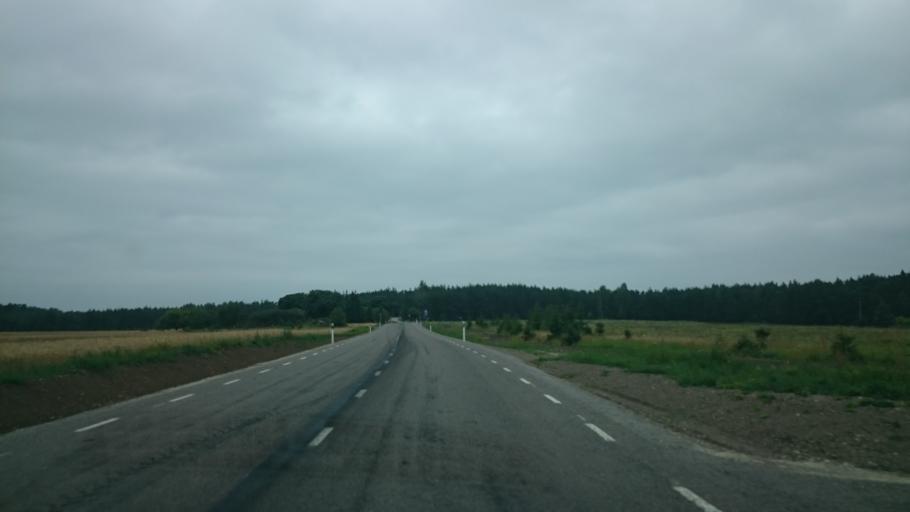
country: EE
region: Saare
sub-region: Orissaare vald
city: Orissaare
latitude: 58.5856
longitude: 22.7064
